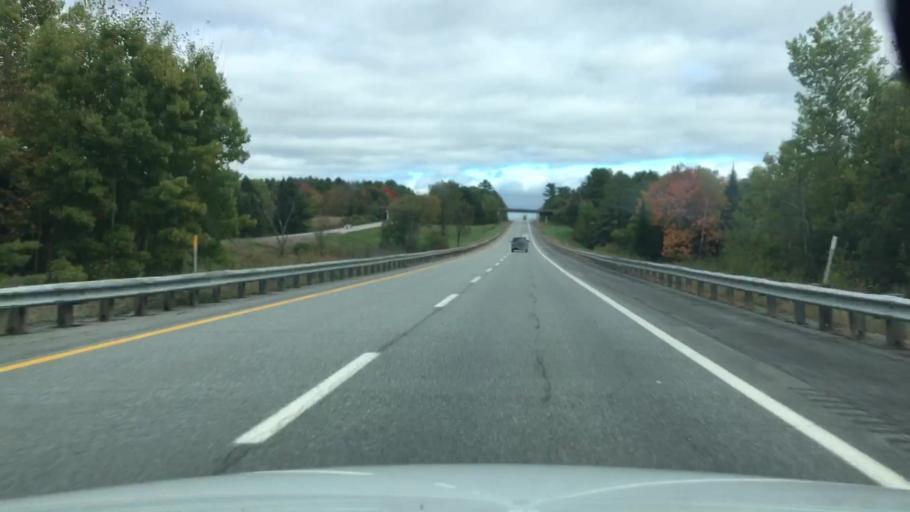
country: US
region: Maine
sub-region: Penobscot County
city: Carmel
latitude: 44.7789
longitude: -69.0675
